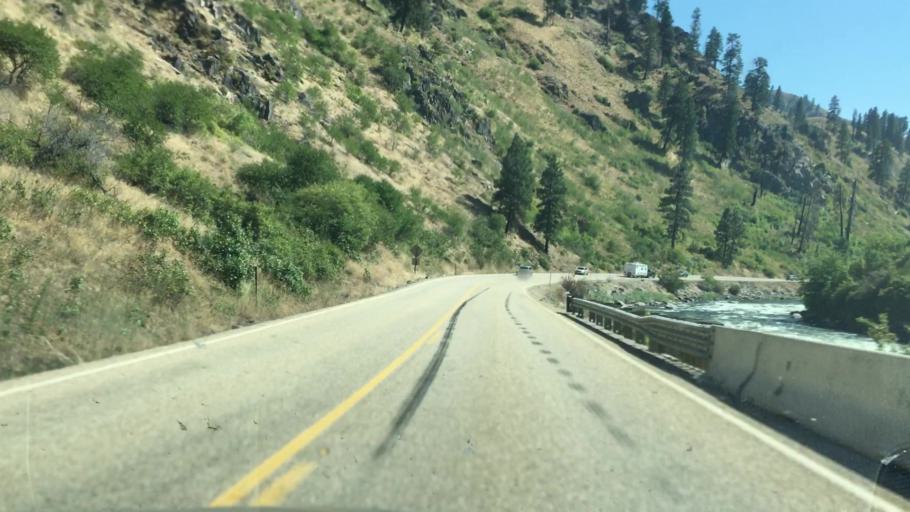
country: US
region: Idaho
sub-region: Boise County
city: Idaho City
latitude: 44.0980
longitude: -116.0999
